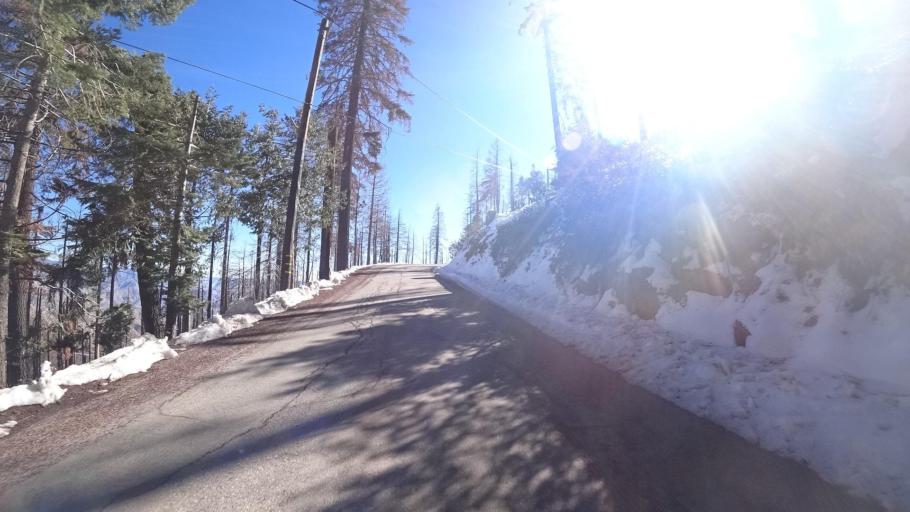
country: US
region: California
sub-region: Kern County
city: Alta Sierra
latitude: 35.7186
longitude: -118.5547
